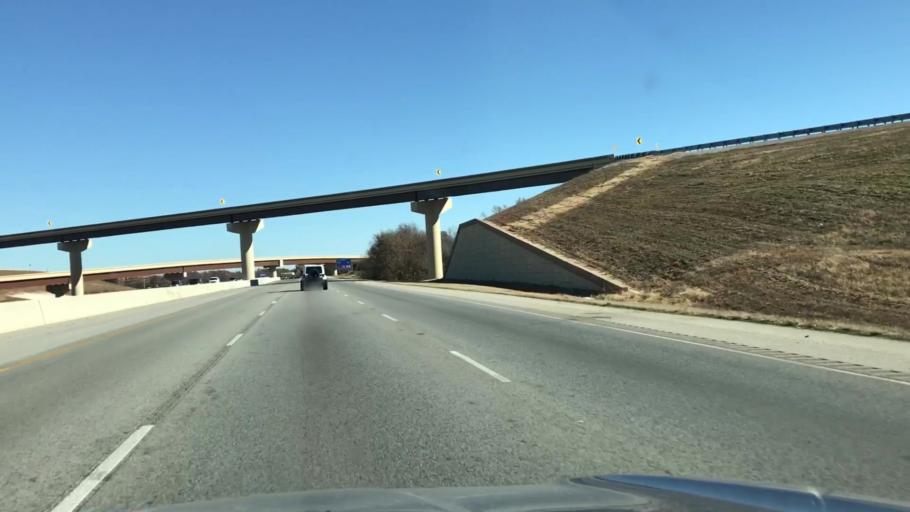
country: US
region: Arkansas
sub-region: Benton County
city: Lowell
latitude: 36.2368
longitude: -94.1623
